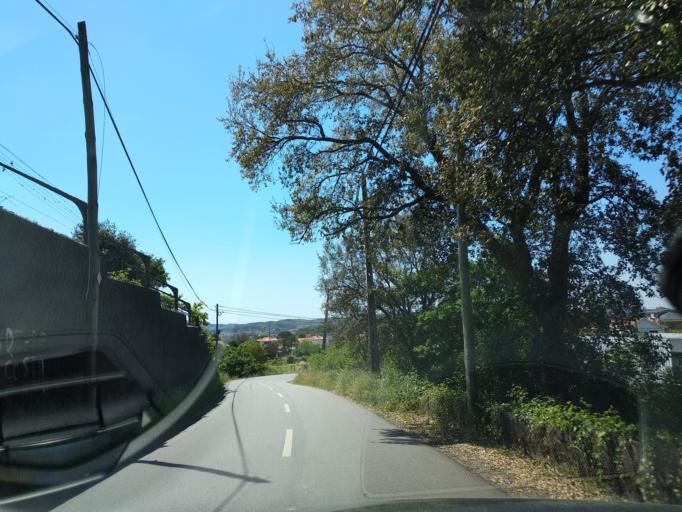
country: PT
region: Porto
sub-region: Paredes
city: Gandra
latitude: 41.1849
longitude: -8.4250
